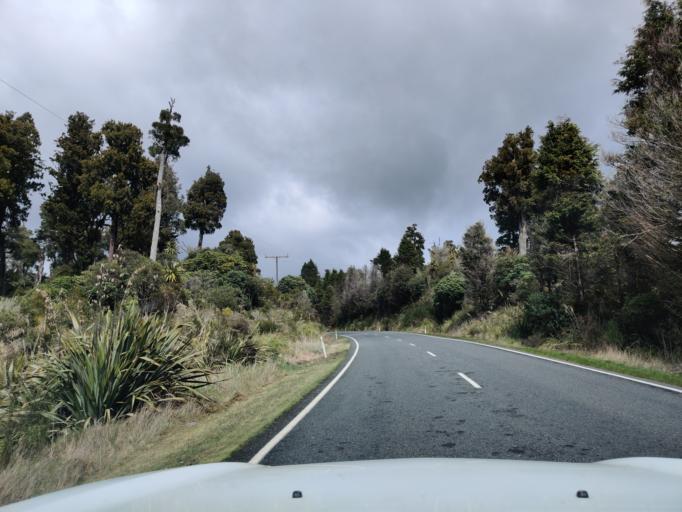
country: NZ
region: Manawatu-Wanganui
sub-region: Ruapehu District
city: Waiouru
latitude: -39.2353
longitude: 175.3918
